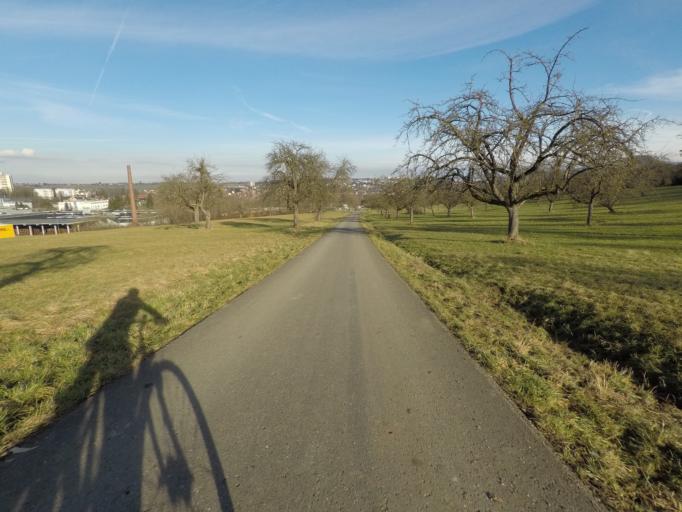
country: DE
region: Baden-Wuerttemberg
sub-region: Tuebingen Region
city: Wannweil
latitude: 48.4912
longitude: 9.1653
